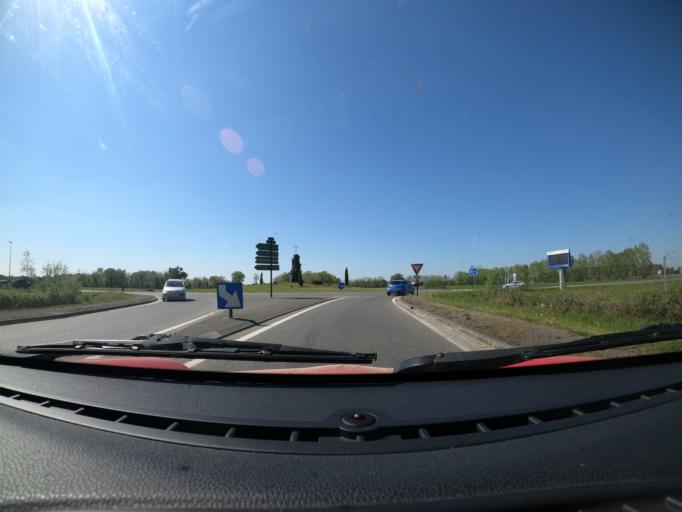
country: FR
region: Aquitaine
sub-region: Departement des Pyrenees-Atlantiques
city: Lescar
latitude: 43.3452
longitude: -0.4219
